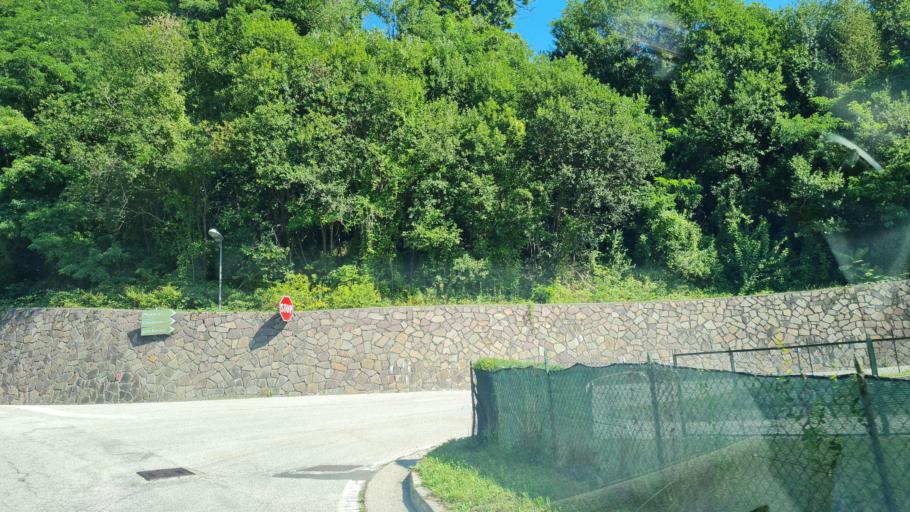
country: IT
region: Trentino-Alto Adige
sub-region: Provincia di Trento
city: Telve di Sopra
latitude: 46.0753
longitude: 11.4733
